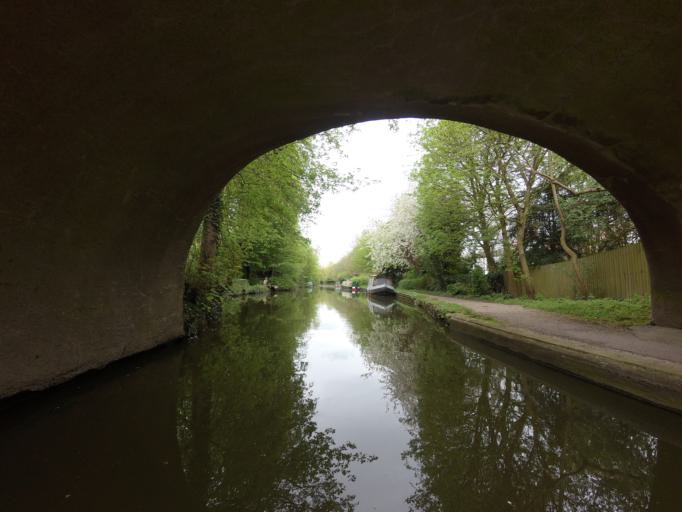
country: GB
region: England
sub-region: Milton Keynes
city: Milton Keynes
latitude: 52.0291
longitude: -0.7309
